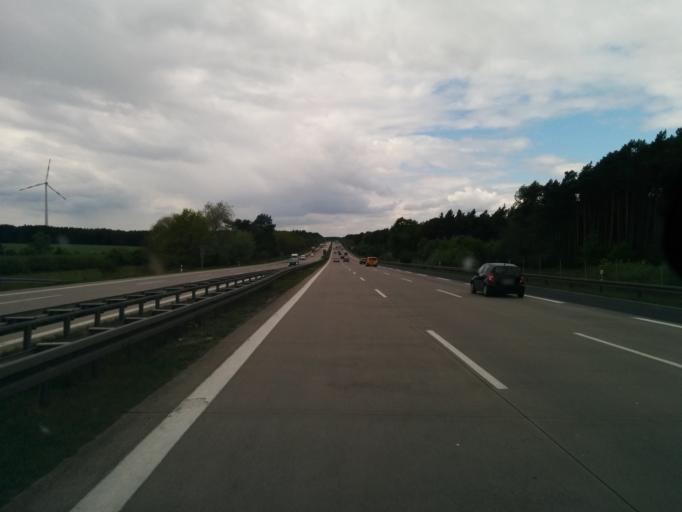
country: DE
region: Brandenburg
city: Golzow
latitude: 52.3405
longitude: 12.6387
